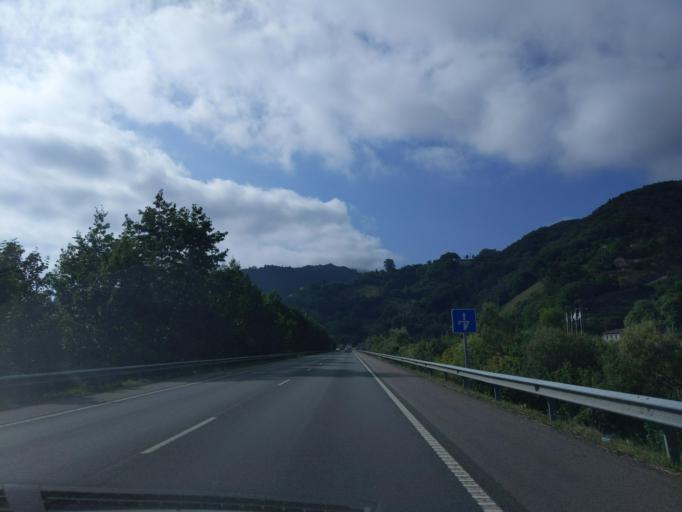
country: ES
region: Asturias
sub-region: Province of Asturias
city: El entrego
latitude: 43.2785
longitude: -5.6171
